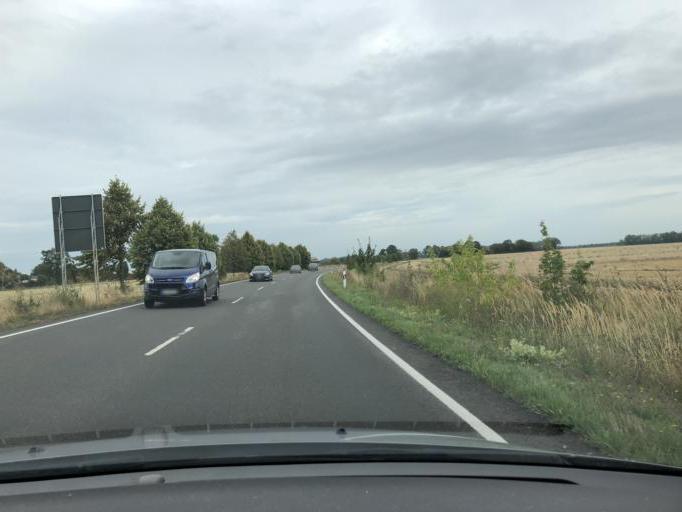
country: DE
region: Saxony-Anhalt
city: Wanzleben
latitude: 52.0739
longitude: 11.4781
